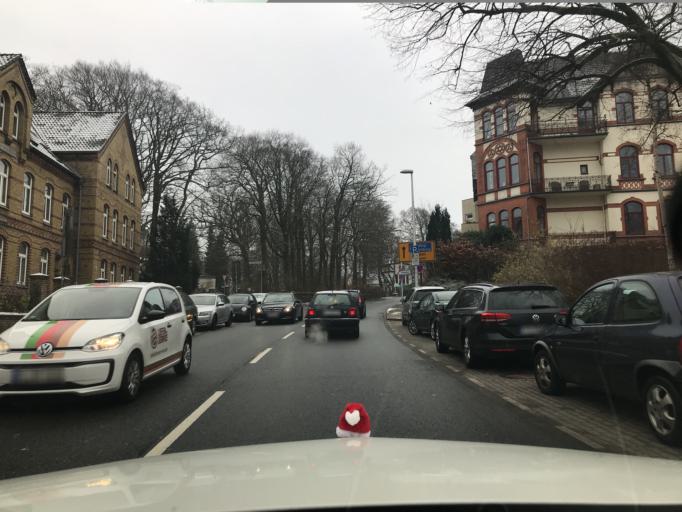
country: DE
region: Schleswig-Holstein
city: Flensburg
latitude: 54.7881
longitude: 9.4281
